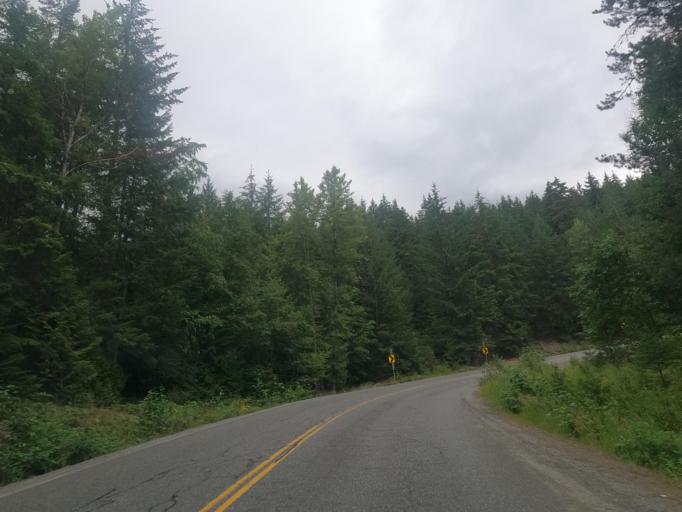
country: CA
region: British Columbia
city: Pemberton
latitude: 50.3027
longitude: -122.5773
